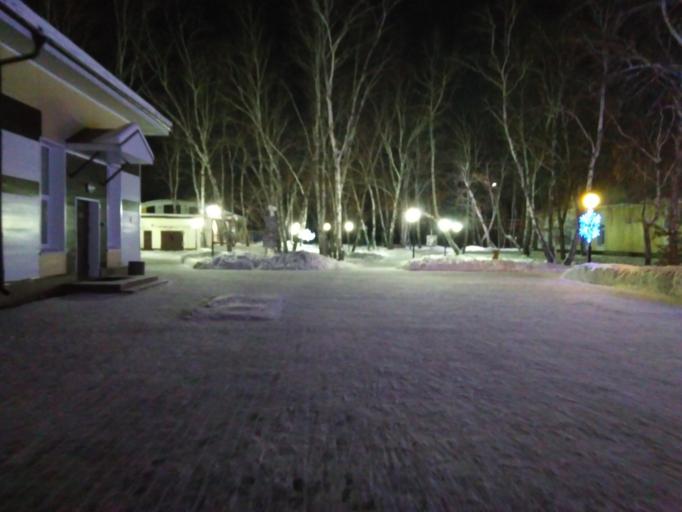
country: RU
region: Omsk
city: Krasnoyarka
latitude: 55.3351
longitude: 73.1232
